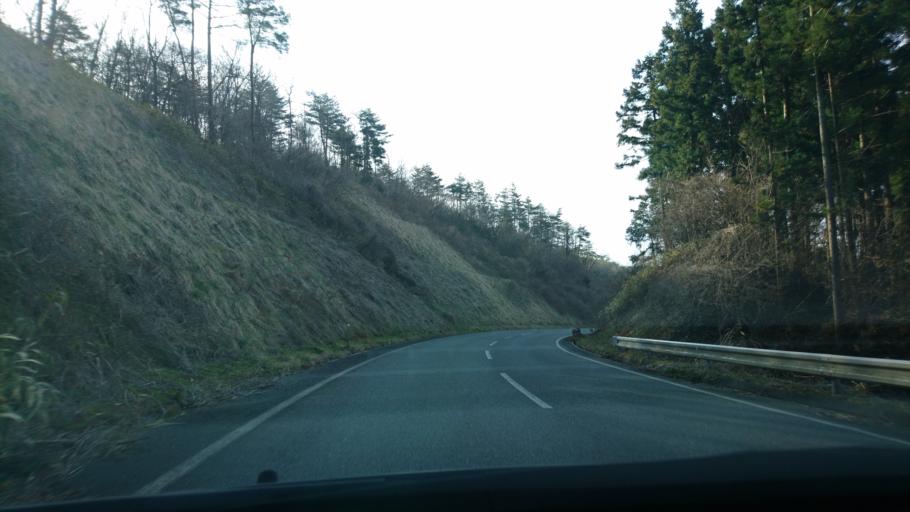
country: JP
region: Iwate
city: Ichinoseki
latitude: 38.8409
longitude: 141.2167
